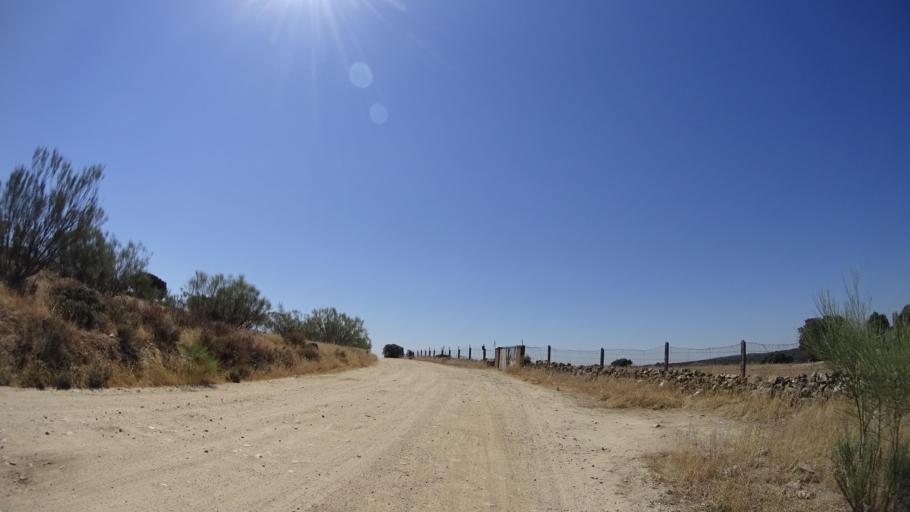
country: ES
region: Madrid
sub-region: Provincia de Madrid
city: Colmenarejo
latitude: 40.5216
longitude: -4.0118
